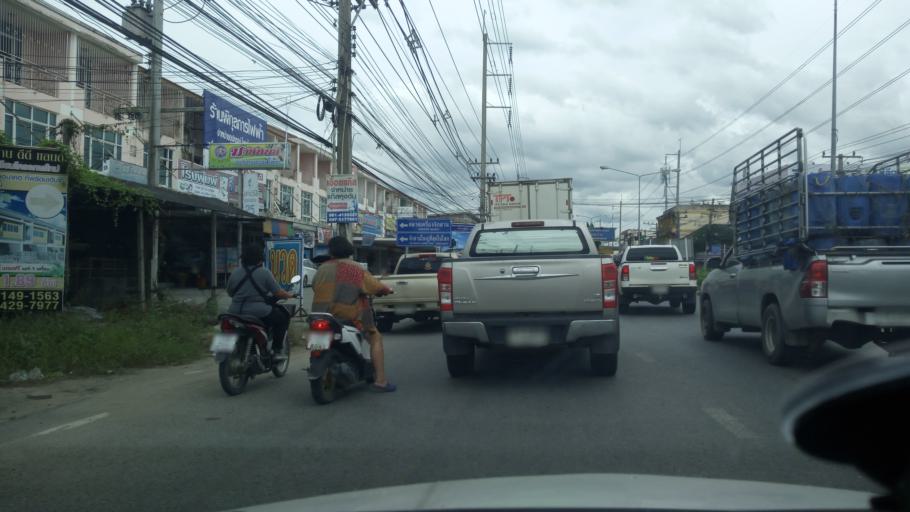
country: TH
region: Chon Buri
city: Phanat Nikhom
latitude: 13.4587
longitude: 101.1738
